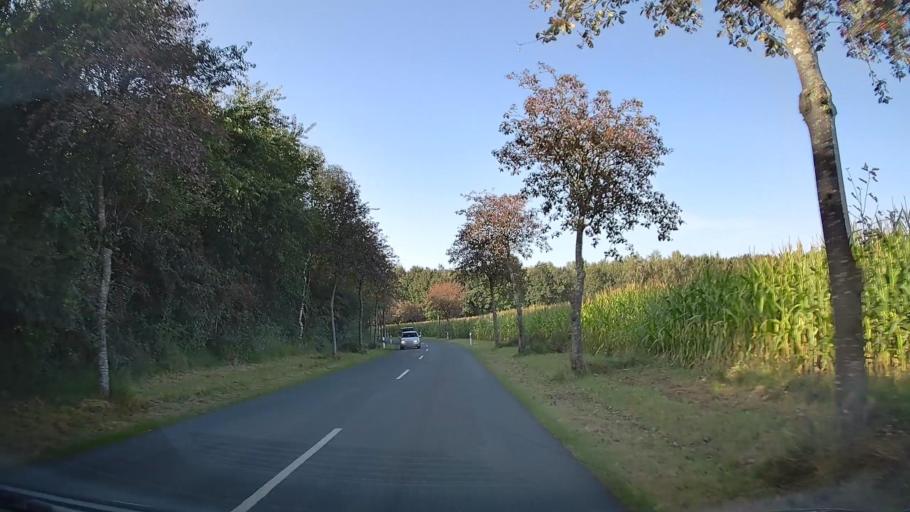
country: DE
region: Lower Saxony
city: Nordholz
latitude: 53.8018
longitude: 8.6089
